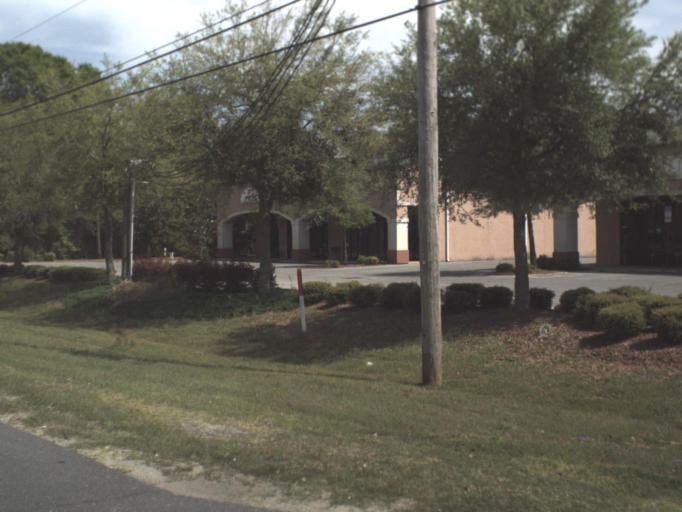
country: US
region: Florida
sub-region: Santa Rosa County
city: Bagdad
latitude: 30.6026
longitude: -87.0853
